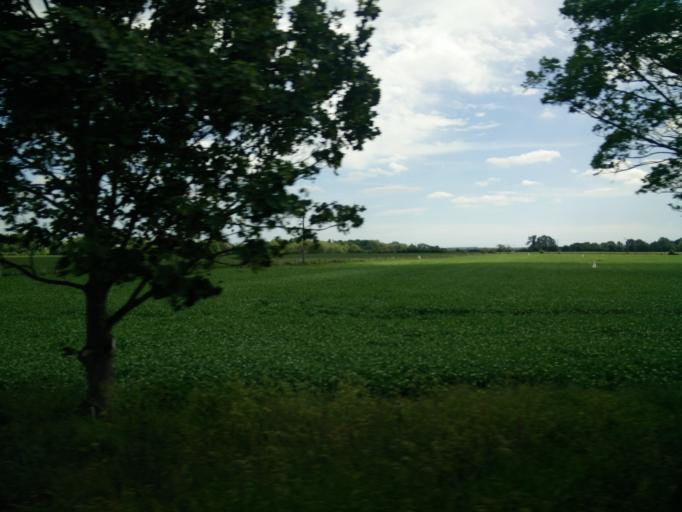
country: GB
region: England
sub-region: Cambridgeshire
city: Harston
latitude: 52.1223
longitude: 0.0584
